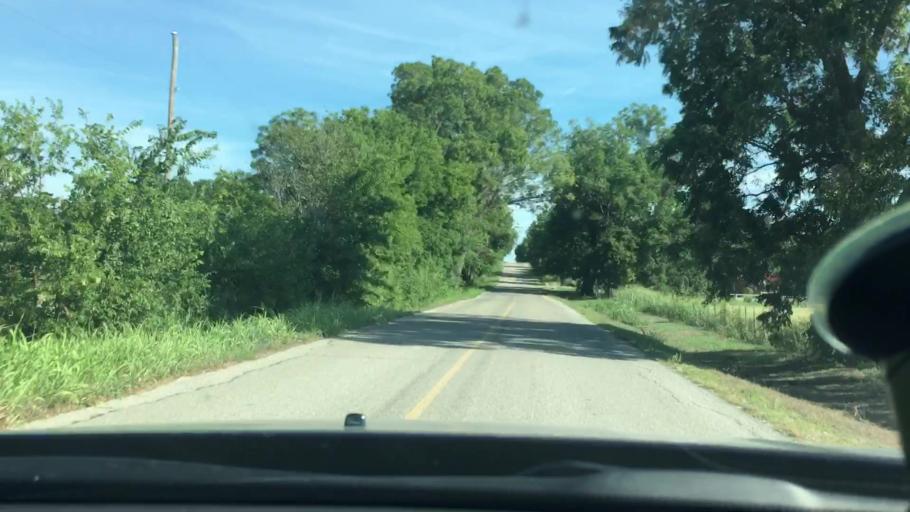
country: US
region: Oklahoma
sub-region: Carter County
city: Lone Grove
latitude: 34.2895
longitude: -97.2825
